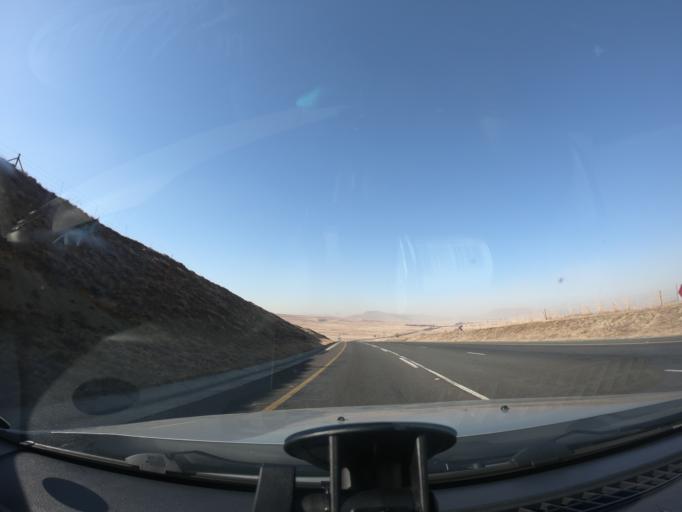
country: ZA
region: Mpumalanga
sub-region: Gert Sibande District Municipality
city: Volksrust
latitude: -27.2118
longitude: 29.8807
